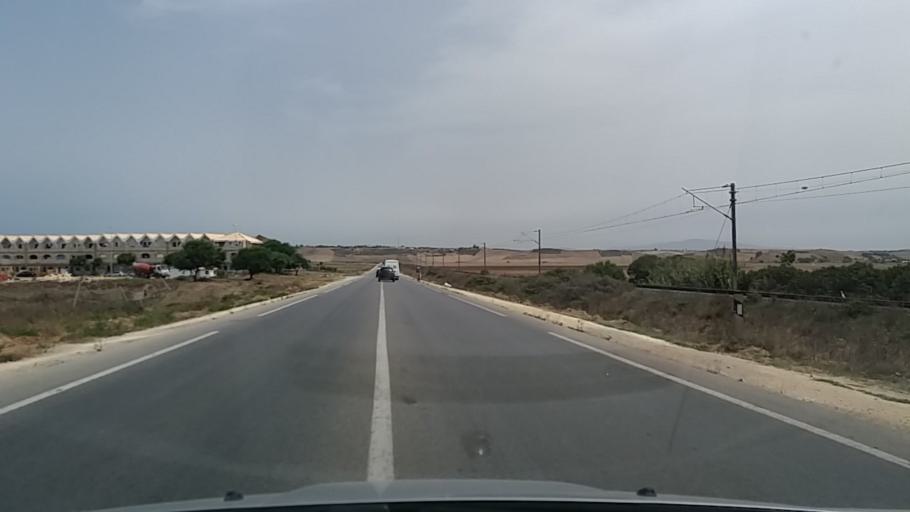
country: MA
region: Tanger-Tetouan
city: Asilah
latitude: 35.4984
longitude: -6.0118
